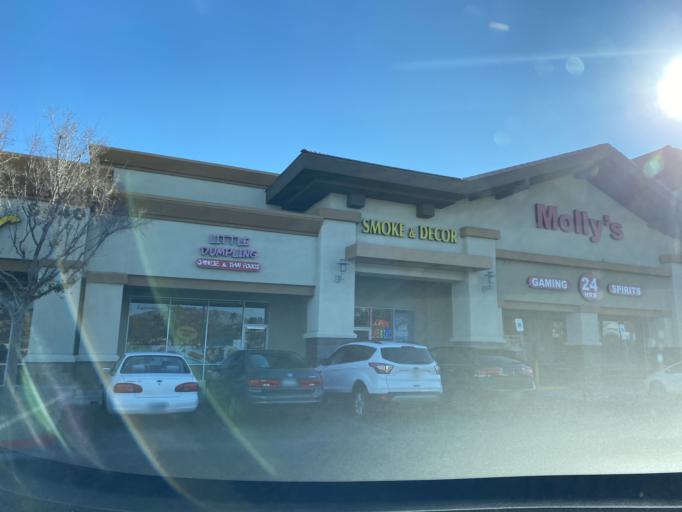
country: US
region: Nevada
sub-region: Clark County
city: Las Vegas
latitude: 36.2797
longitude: -115.2620
